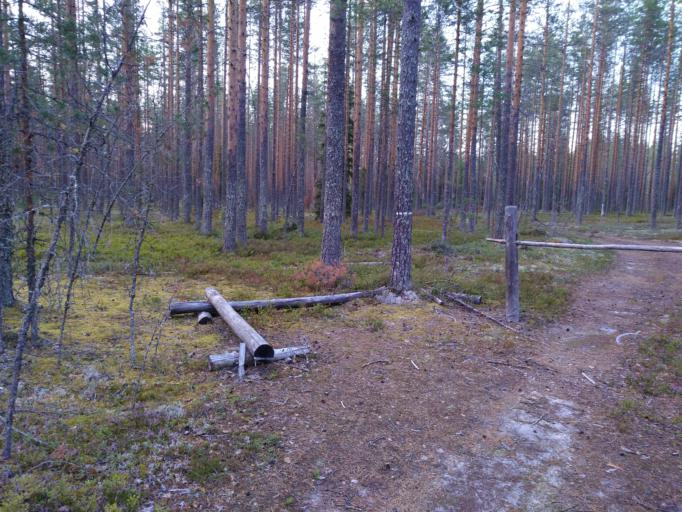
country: FI
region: North Karelia
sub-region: Joensuu
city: Ilomantsi
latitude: 63.1153
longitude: 30.7742
